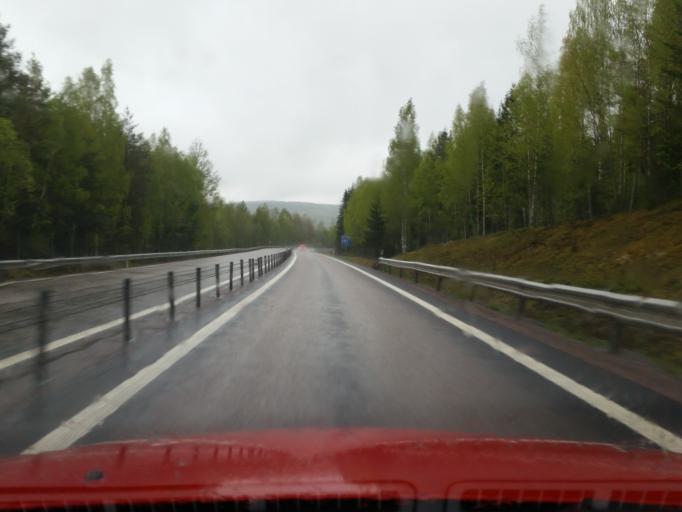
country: SE
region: Dalarna
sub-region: Saters Kommun
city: Saeter
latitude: 60.3584
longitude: 15.7343
